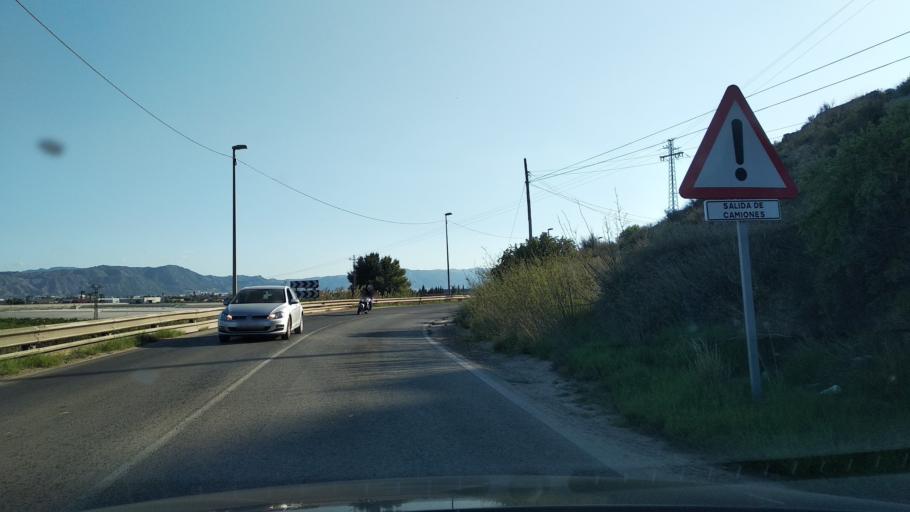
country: ES
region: Murcia
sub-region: Murcia
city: Santomera
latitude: 38.0549
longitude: -1.0527
